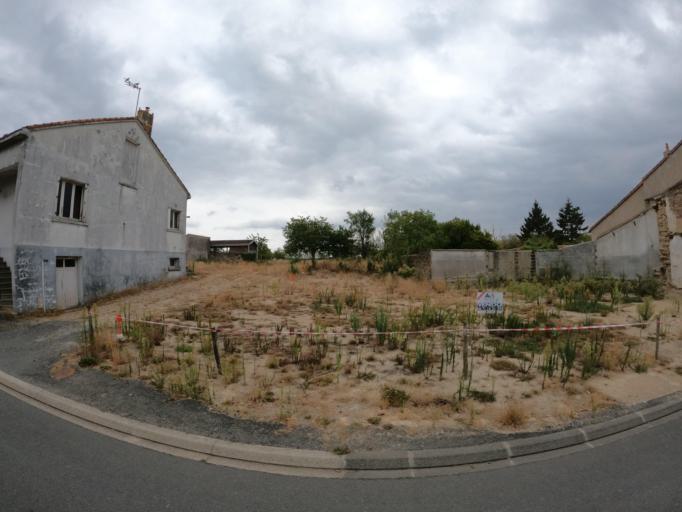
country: FR
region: Pays de la Loire
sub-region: Departement de la Vendee
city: La Boissiere-de-Montaigu
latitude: 46.9809
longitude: -1.1726
